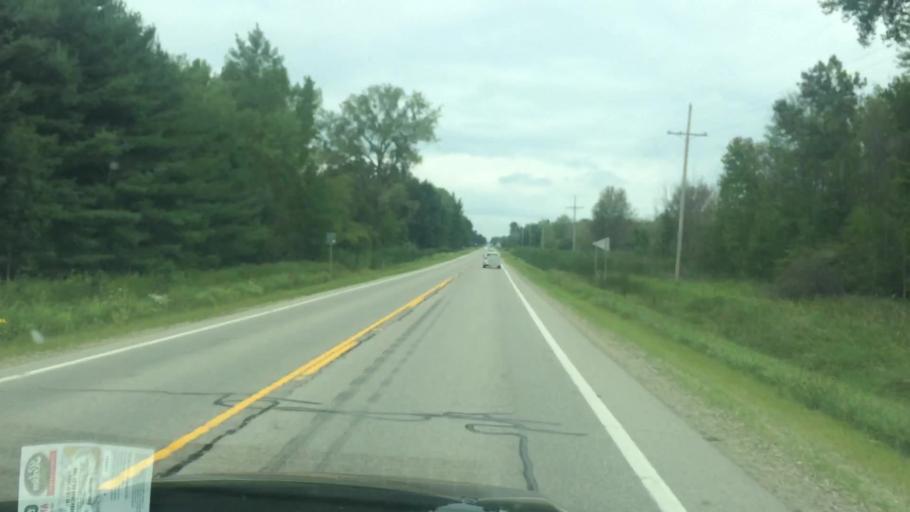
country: US
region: Michigan
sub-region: Sanilac County
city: Marlette
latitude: 43.4449
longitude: -83.0886
